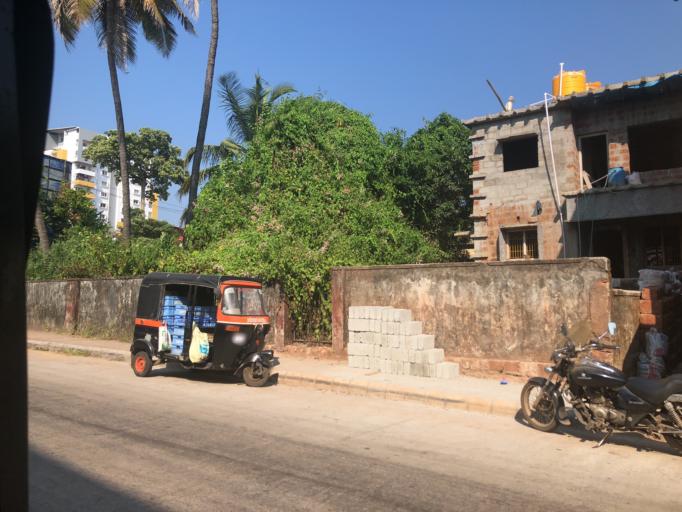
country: IN
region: Karnataka
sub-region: Dakshina Kannada
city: Mangalore
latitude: 12.8802
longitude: 74.8338
